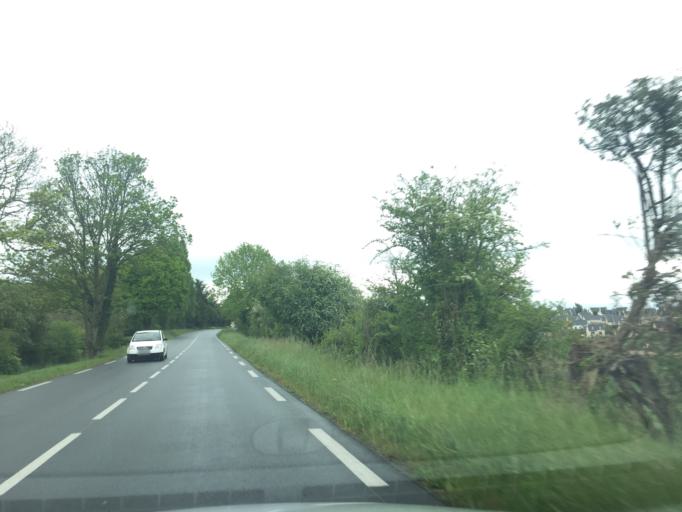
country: FR
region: Brittany
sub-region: Departement des Cotes-d'Armor
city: Crehen
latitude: 48.5411
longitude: -2.2196
